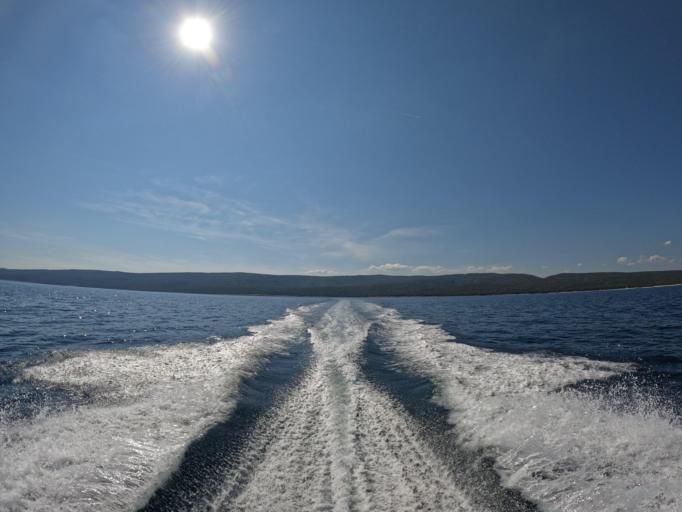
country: HR
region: Primorsko-Goranska
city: Cres
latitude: 44.9454
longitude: 14.4903
